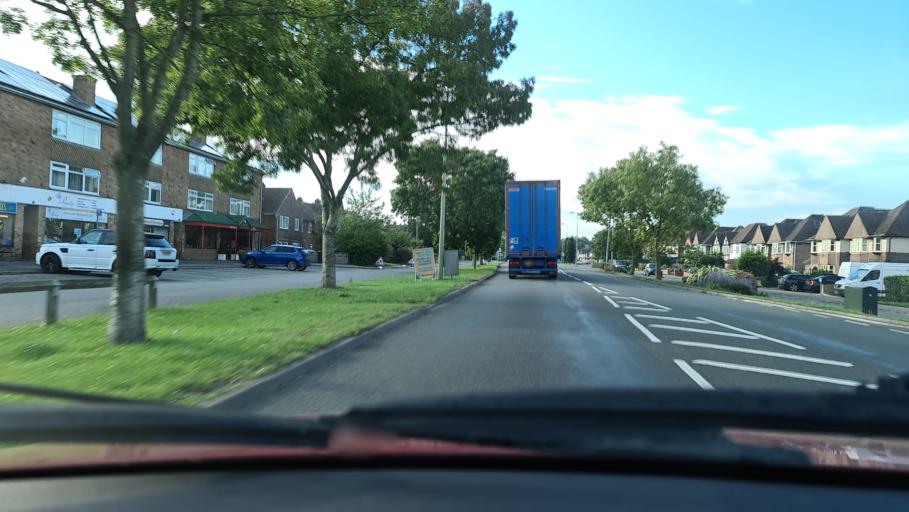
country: GB
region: England
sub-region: Oxfordshire
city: Kidlington
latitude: 51.8120
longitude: -1.2801
